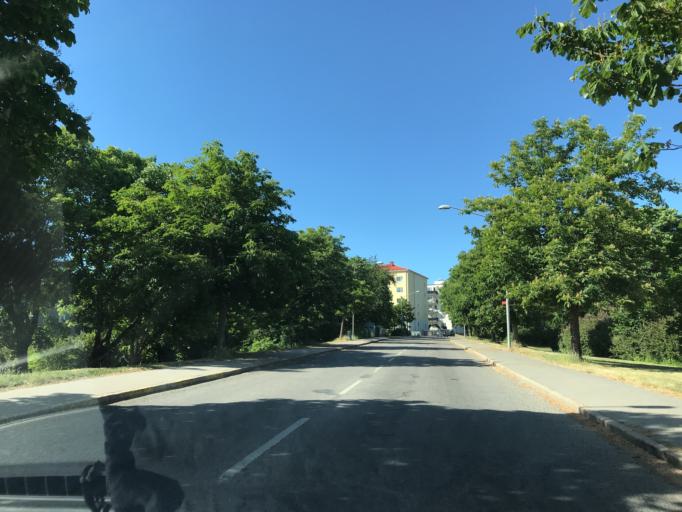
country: SE
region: Stockholm
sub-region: Huddinge Kommun
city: Segeltorp
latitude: 59.2885
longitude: 17.9391
